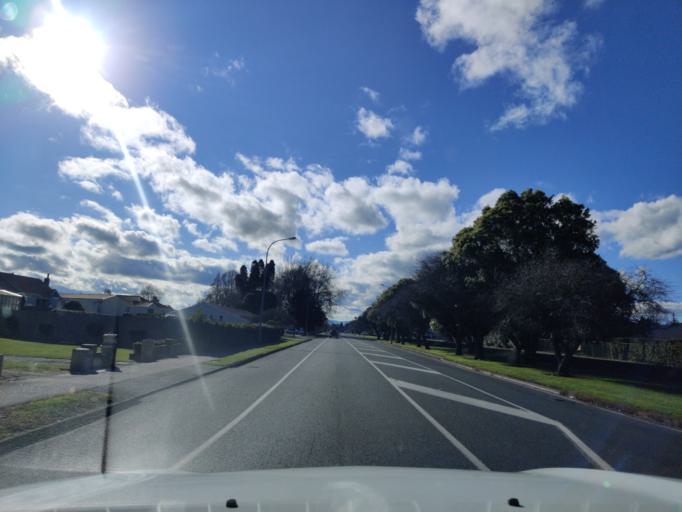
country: NZ
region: Waikato
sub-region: Matamata-Piako District
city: Matamata
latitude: -37.8186
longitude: 175.7711
